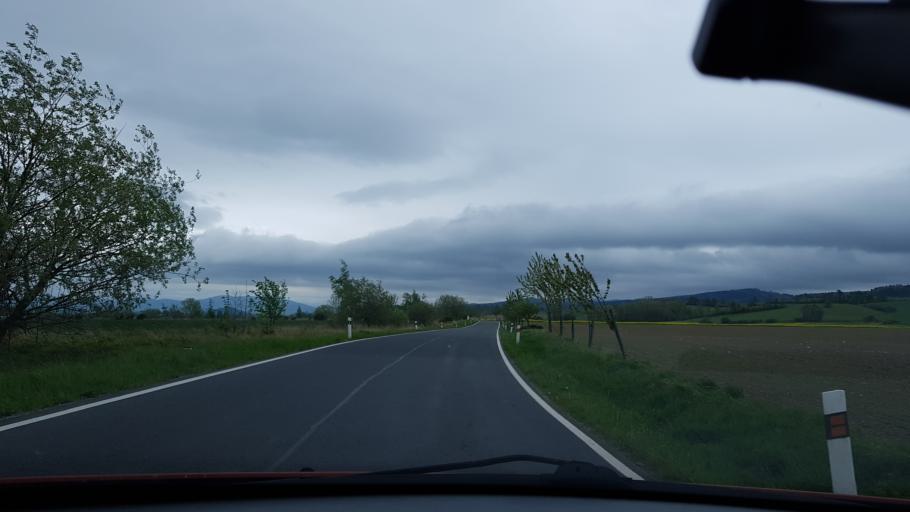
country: PL
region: Opole Voivodeship
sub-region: Powiat nyski
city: Kamienica
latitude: 50.4198
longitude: 16.9729
